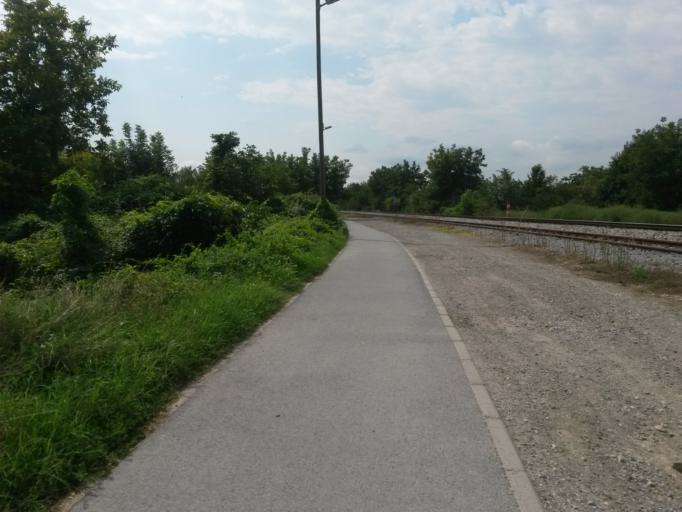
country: HR
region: Osjecko-Baranjska
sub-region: Grad Osijek
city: Osijek
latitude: 45.5507
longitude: 18.6744
